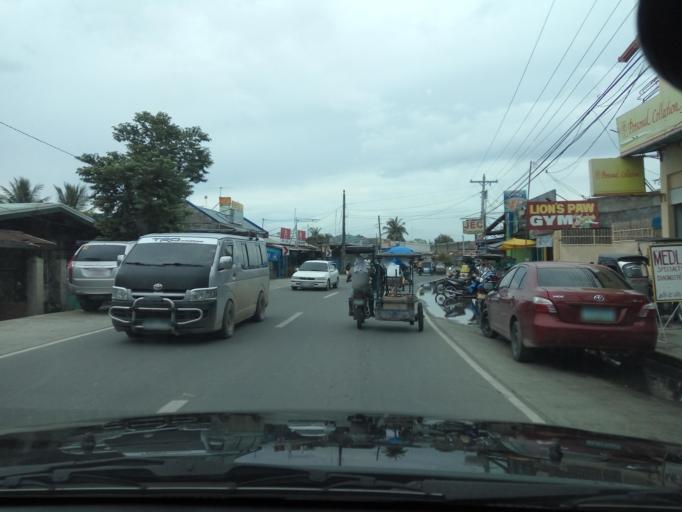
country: PH
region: Central Luzon
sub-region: Province of Nueva Ecija
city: Concepcion
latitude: 15.4492
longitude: 120.7983
